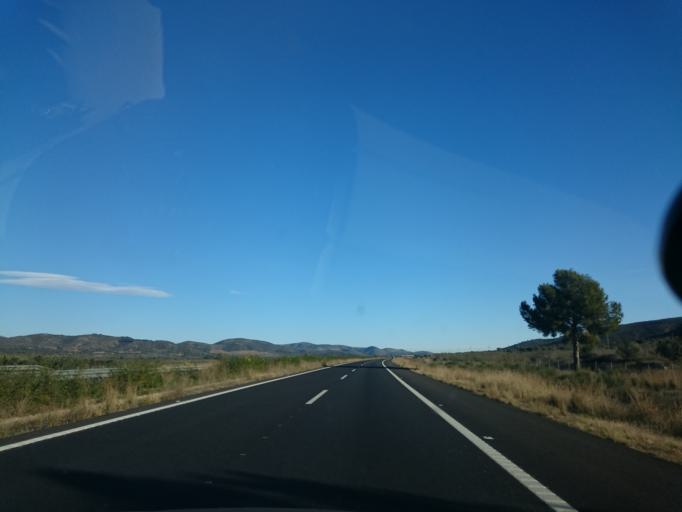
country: ES
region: Valencia
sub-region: Provincia de Castello
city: Alcala de Xivert
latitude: 40.3093
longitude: 0.2414
